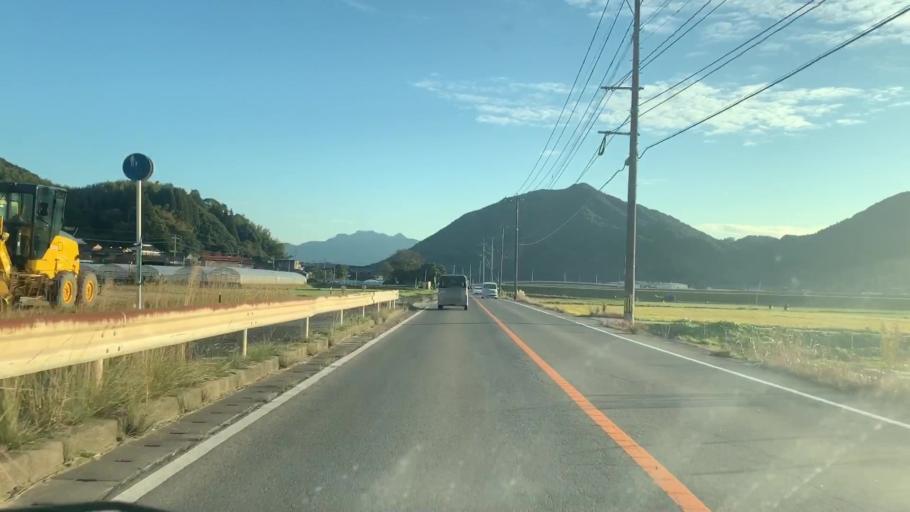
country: JP
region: Saga Prefecture
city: Karatsu
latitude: 33.3794
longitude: 129.9993
